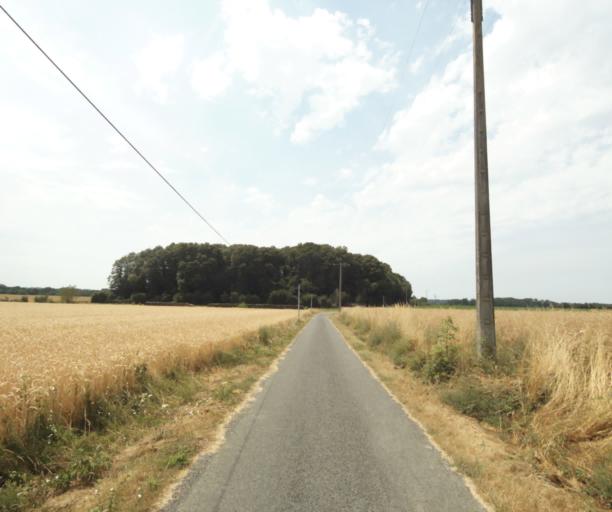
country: FR
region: Centre
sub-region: Departement d'Eure-et-Loir
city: La Bazoche-Gouet
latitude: 48.1886
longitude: 0.9499
